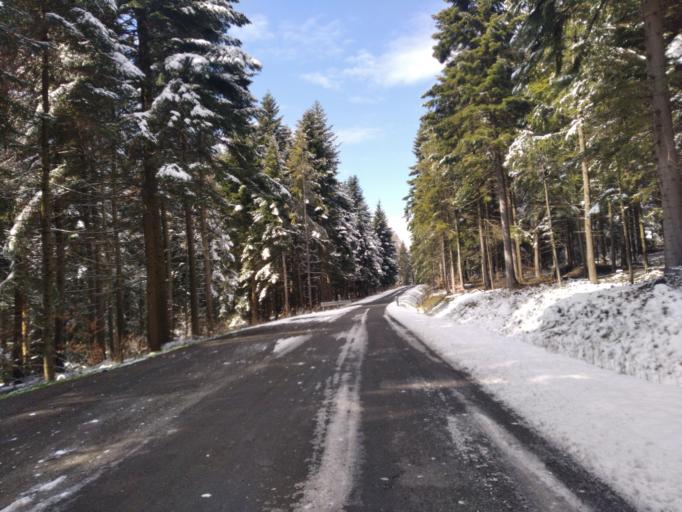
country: PL
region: Subcarpathian Voivodeship
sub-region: Powiat ropczycko-sedziszowski
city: Ropczyce
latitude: 50.0152
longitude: 21.6059
